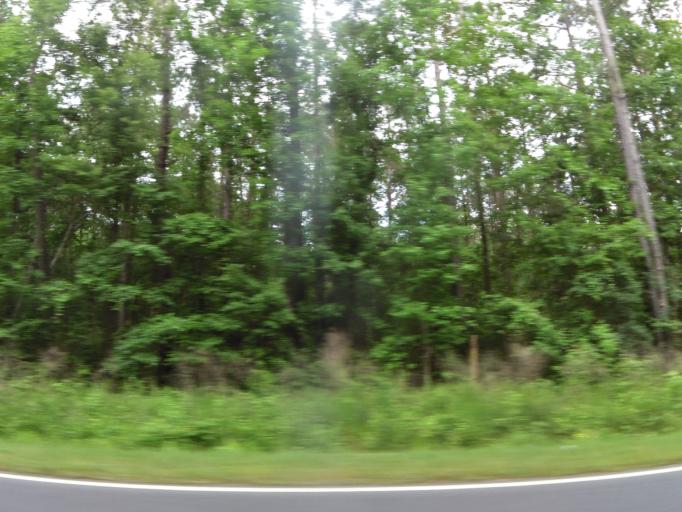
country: US
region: South Carolina
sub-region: Jasper County
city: Ridgeland
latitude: 32.4597
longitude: -81.1068
